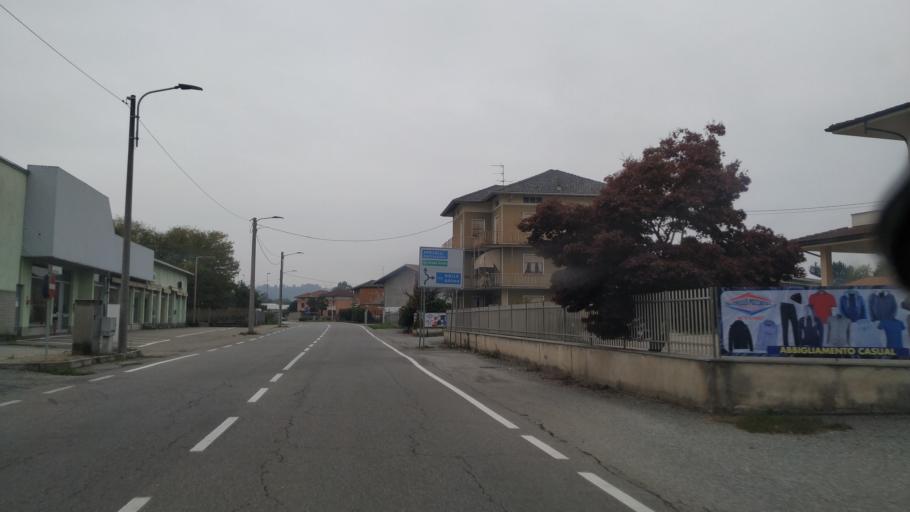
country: IT
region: Piedmont
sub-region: Provincia di Biella
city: Cerreto Castello
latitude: 45.5604
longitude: 8.1725
